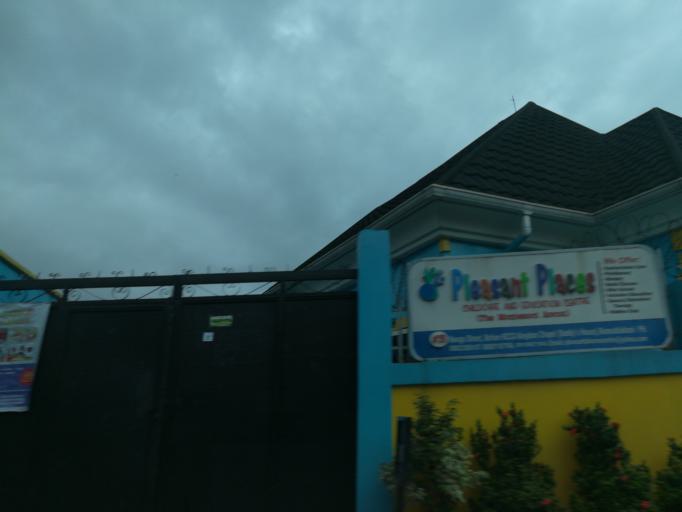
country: NG
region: Rivers
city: Port Harcourt
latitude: 4.8371
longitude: 7.0272
